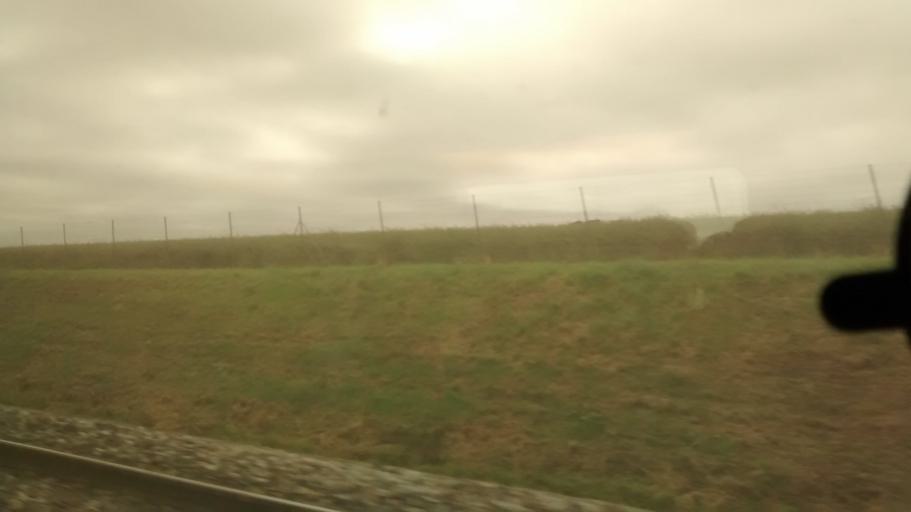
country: FR
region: Centre
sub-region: Departement du Loir-et-Cher
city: Droue
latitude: 48.0742
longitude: 1.0633
